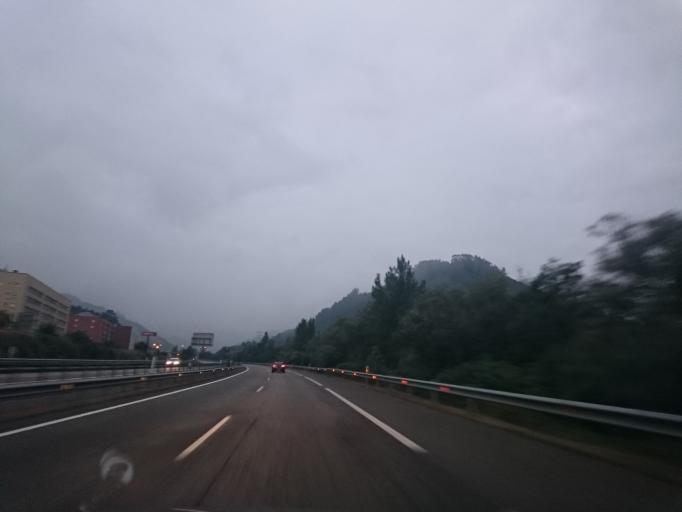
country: ES
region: Asturias
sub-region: Province of Asturias
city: Mieres
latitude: 43.2283
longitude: -5.7832
